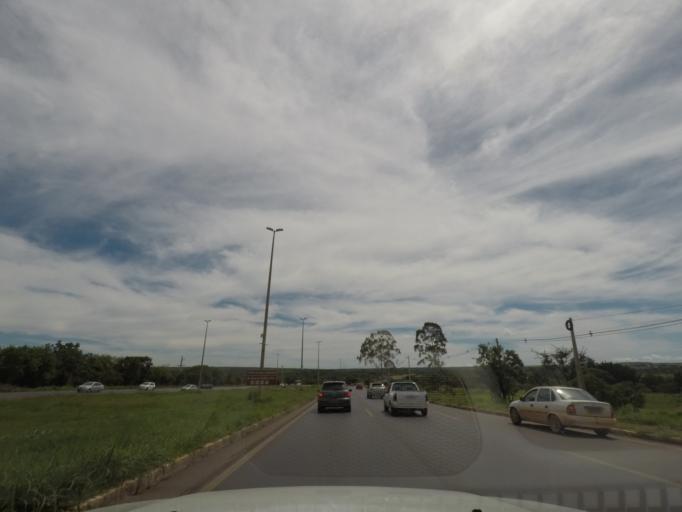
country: BR
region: Goias
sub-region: Planaltina
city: Planaltina
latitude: -15.5978
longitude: -47.6745
